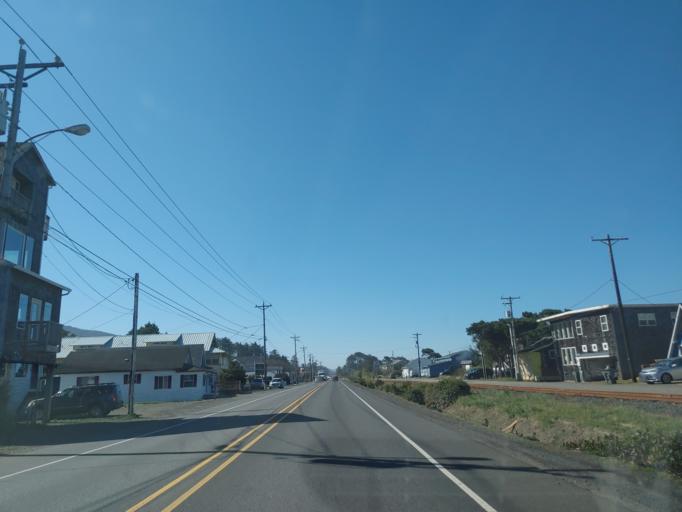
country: US
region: Oregon
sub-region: Tillamook County
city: Rockaway Beach
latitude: 45.6072
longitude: -123.9449
